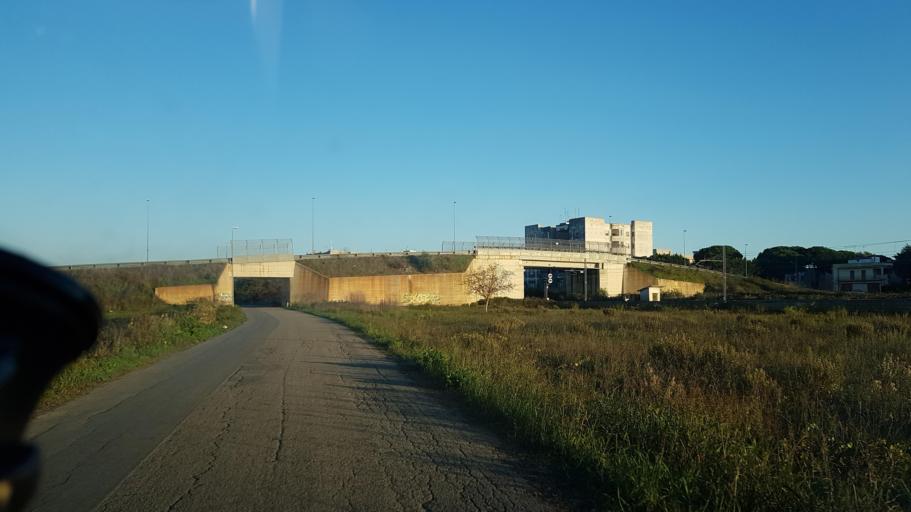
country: IT
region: Apulia
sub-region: Provincia di Brindisi
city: Mesagne
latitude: 40.5609
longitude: 17.7932
